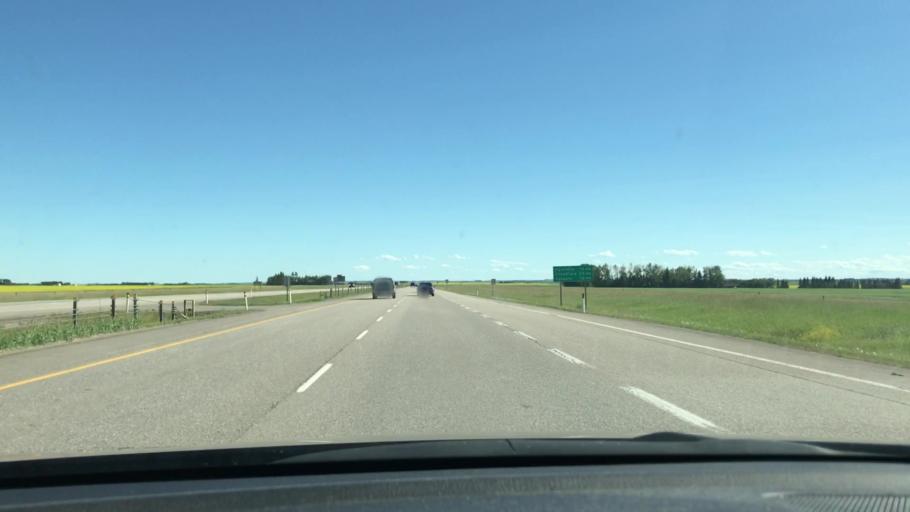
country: CA
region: Alberta
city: Didsbury
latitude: 51.6570
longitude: -114.0256
